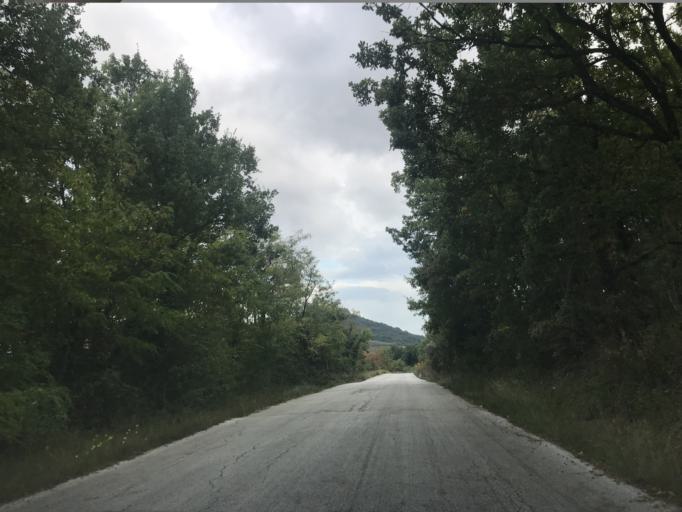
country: IT
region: Molise
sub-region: Provincia di Campobasso
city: Duronia
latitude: 41.6780
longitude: 14.4533
